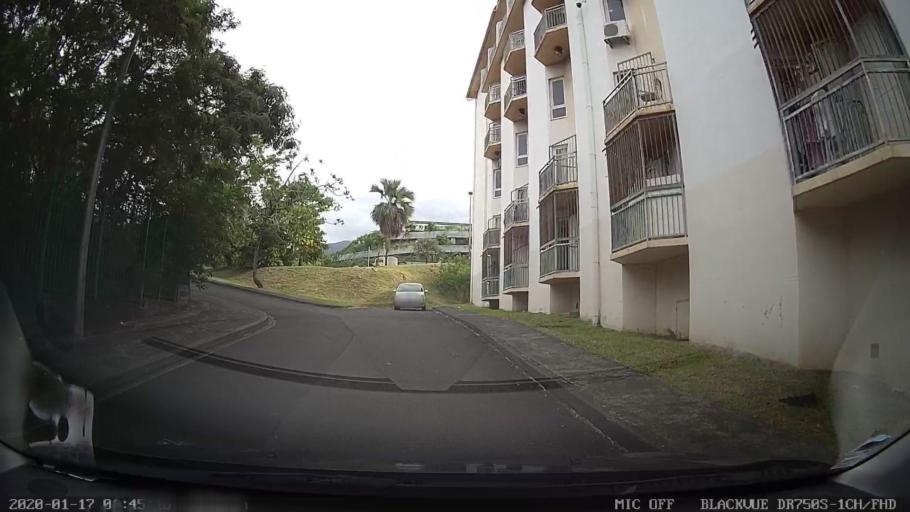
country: RE
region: Reunion
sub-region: Reunion
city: Saint-Denis
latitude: -20.9016
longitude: 55.4863
